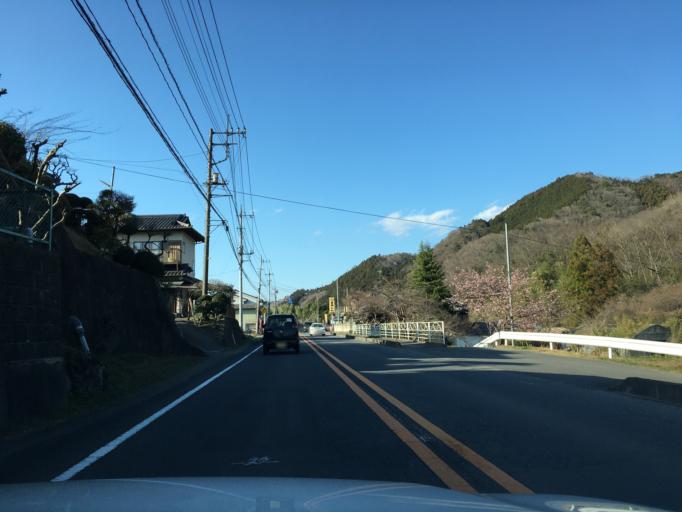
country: JP
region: Ibaraki
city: Omiya
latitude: 36.6532
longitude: 140.3933
